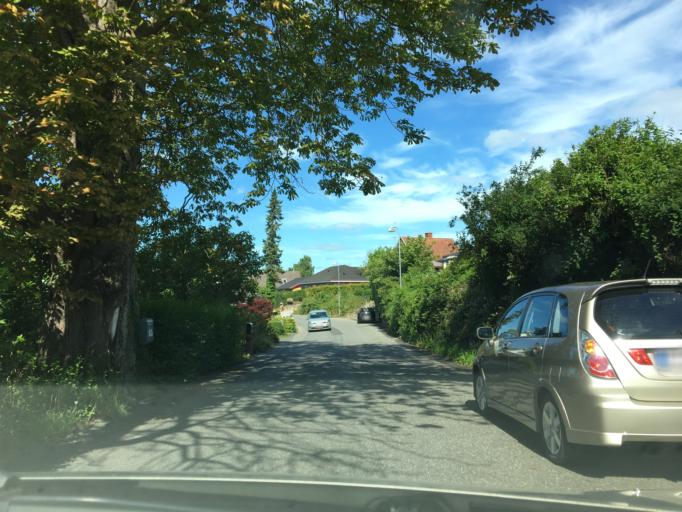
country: DK
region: South Denmark
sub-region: Svendborg Kommune
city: Thuro By
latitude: 55.0474
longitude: 10.6672
